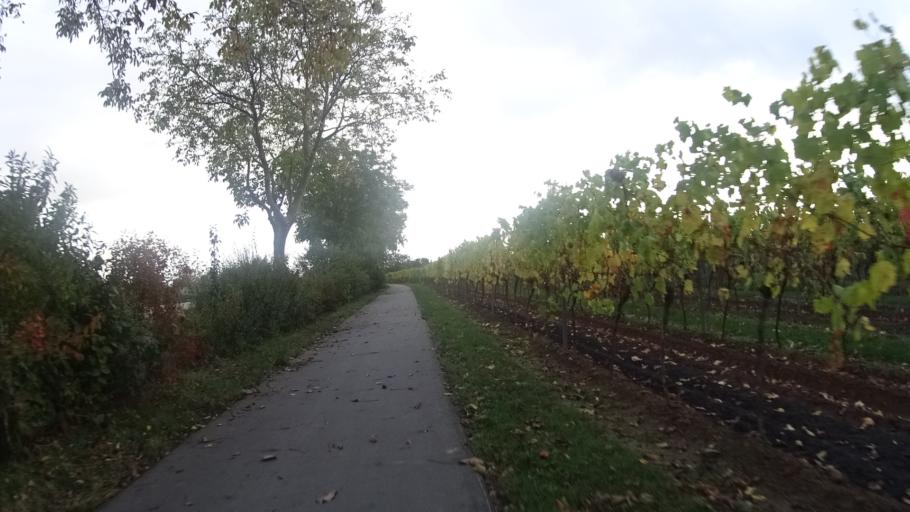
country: DE
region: Rheinland-Pfalz
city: Meckenheim
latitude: 49.3955
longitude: 8.2433
